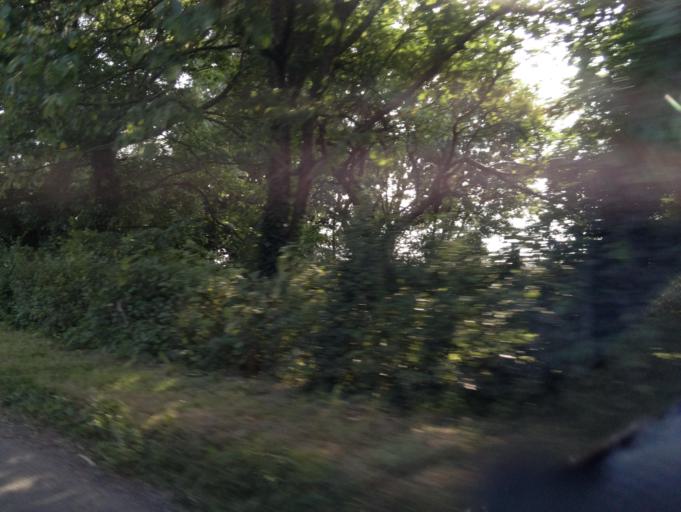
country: GB
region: England
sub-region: Devon
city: Bradninch
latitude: 50.8078
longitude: -3.4989
